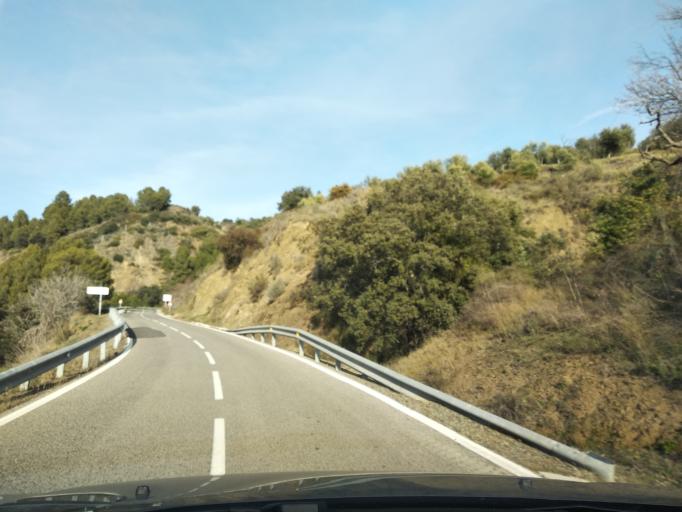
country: ES
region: Catalonia
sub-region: Provincia de Tarragona
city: Margalef
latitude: 41.2280
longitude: 0.7795
